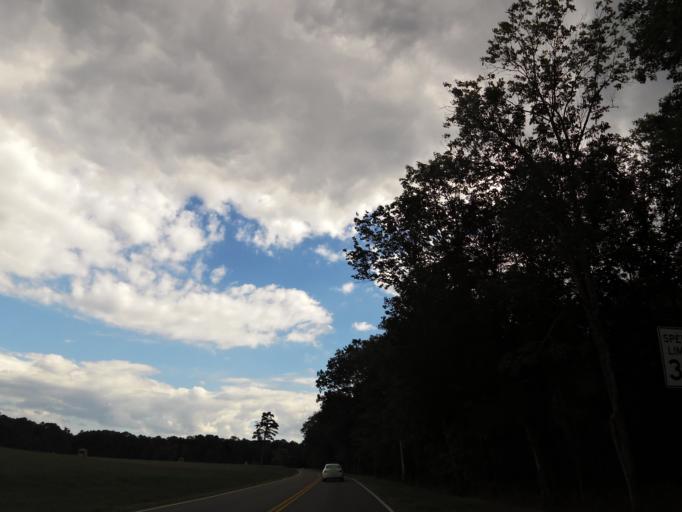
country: US
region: Georgia
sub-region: Catoosa County
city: Fort Oglethorpe
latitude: 34.9321
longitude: -85.2597
